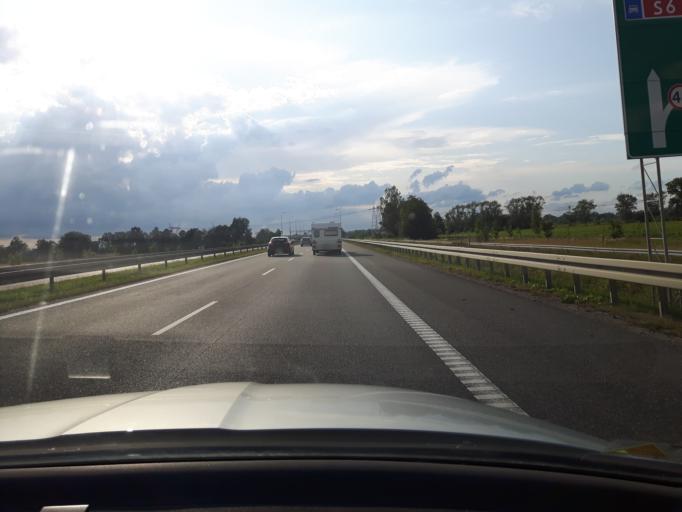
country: PL
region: Pomeranian Voivodeship
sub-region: Powiat gdanski
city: Suchy Dab
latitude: 54.3132
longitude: 18.7630
